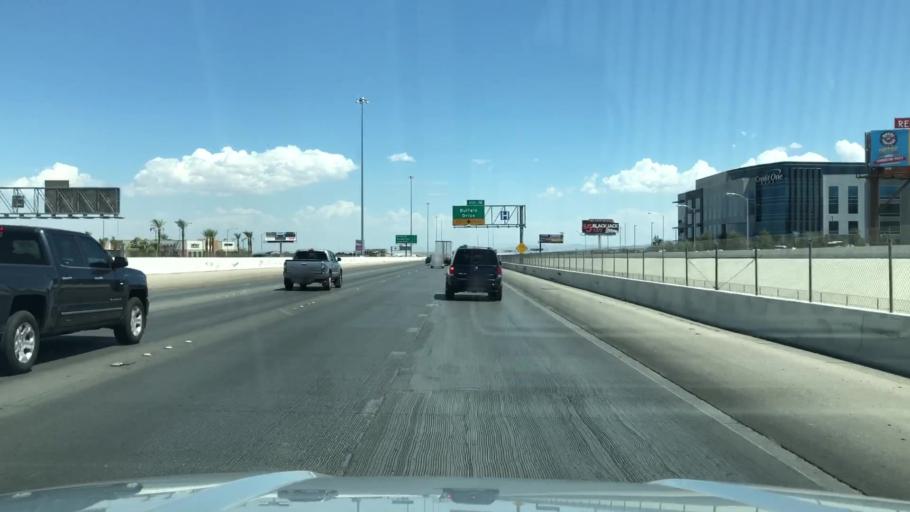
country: US
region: Nevada
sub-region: Clark County
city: Spring Valley
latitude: 36.0660
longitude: -115.2736
